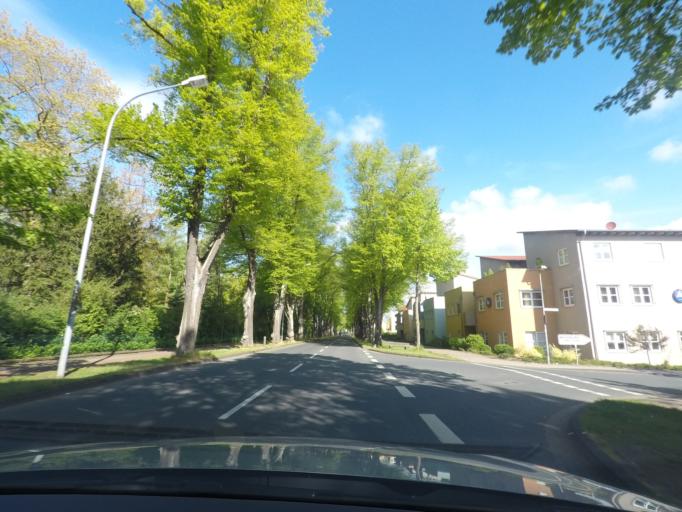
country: DE
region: Lower Saxony
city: Helmstedt
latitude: 52.2195
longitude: 11.0261
